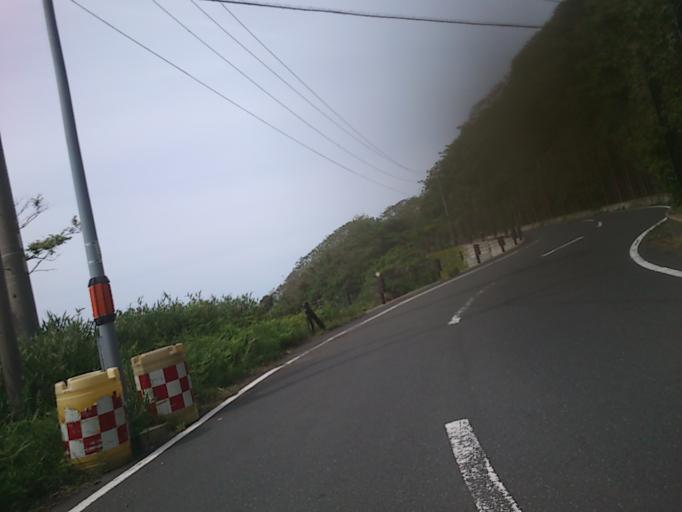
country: JP
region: Hyogo
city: Toyooka
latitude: 35.6910
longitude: 135.0022
